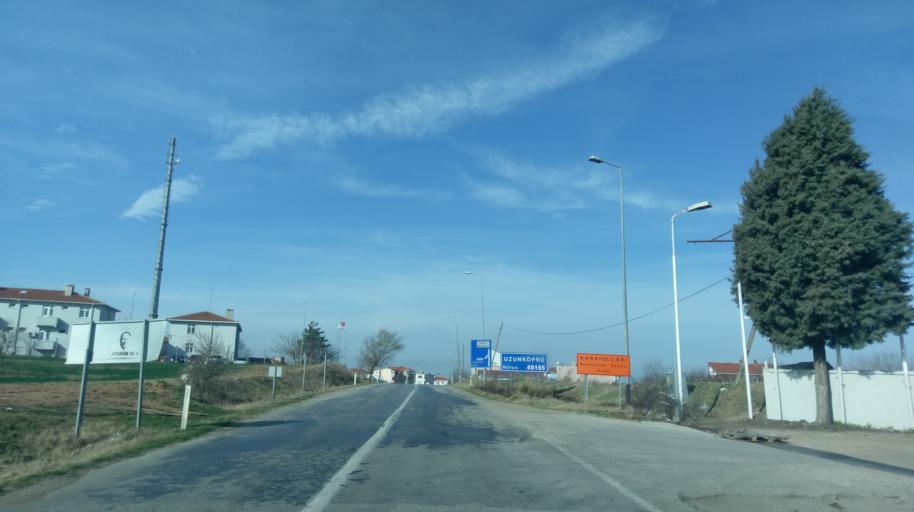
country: TR
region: Edirne
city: Uzun Keupru
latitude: 41.2677
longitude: 26.7089
